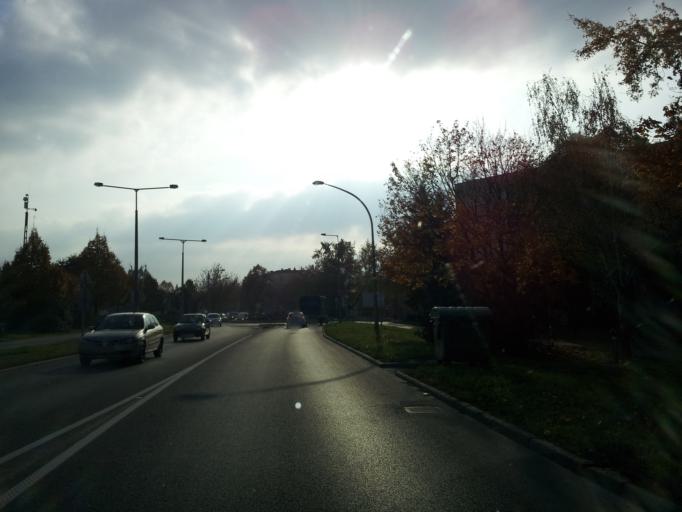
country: HU
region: Komarom-Esztergom
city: Oroszlany
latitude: 47.4908
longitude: 18.3179
